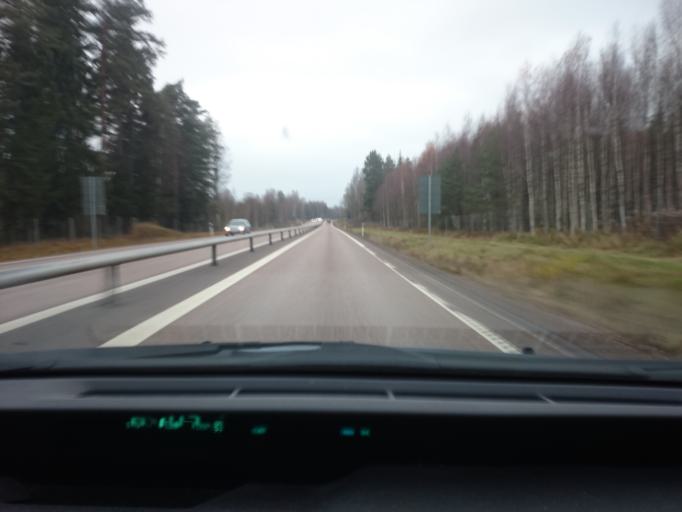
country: SE
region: Dalarna
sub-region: Avesta Kommun
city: Avesta
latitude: 60.1656
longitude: 16.1542
